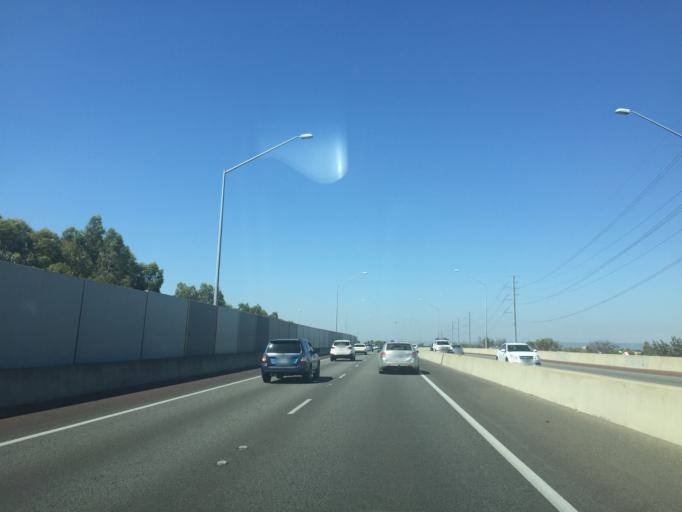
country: AU
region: Western Australia
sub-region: Canning
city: Willetton
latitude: -32.0710
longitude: 115.8882
